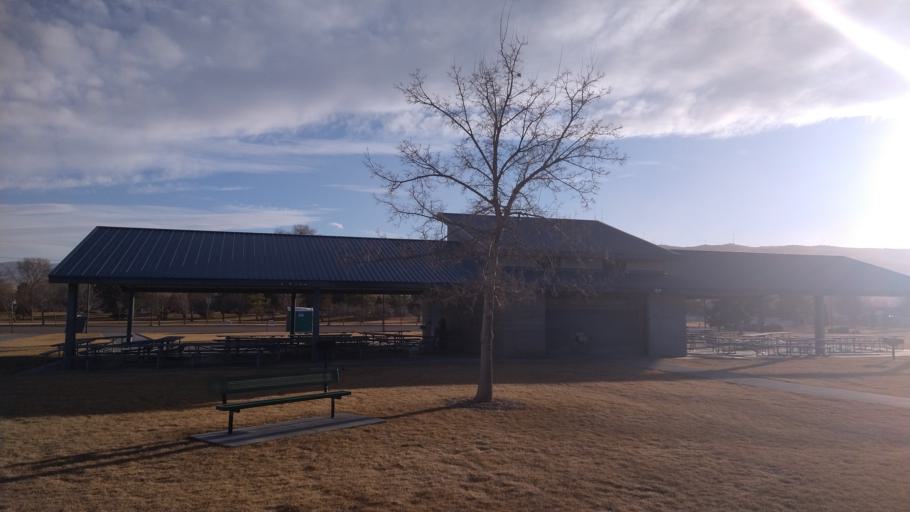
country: US
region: Idaho
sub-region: Bannock County
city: Chubbuck
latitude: 42.9072
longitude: -112.4828
